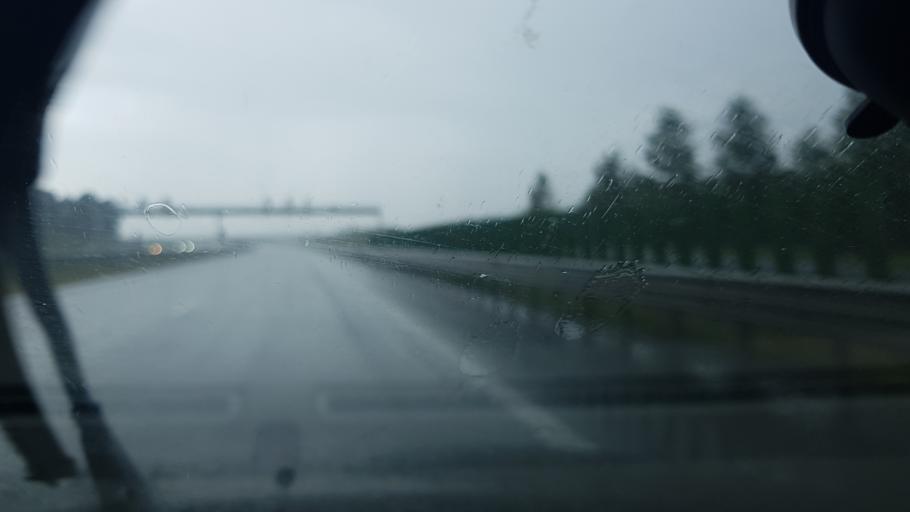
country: PL
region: Warmian-Masurian Voivodeship
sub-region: Powiat olsztynski
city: Olsztynek
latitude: 53.4851
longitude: 20.3209
